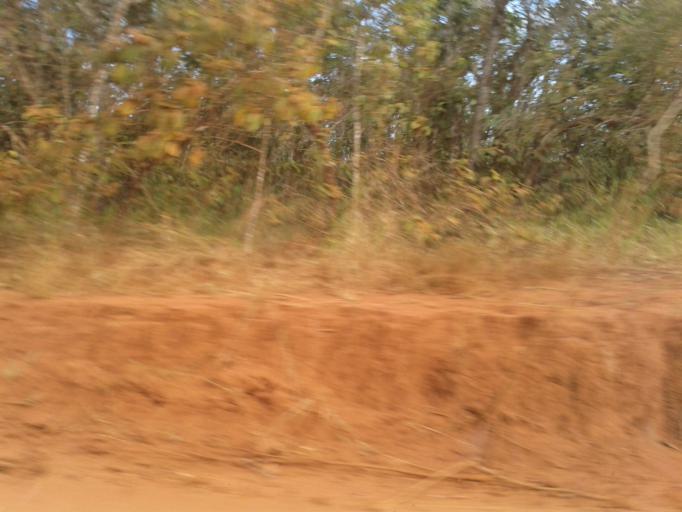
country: BR
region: Minas Gerais
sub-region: Ituiutaba
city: Ituiutaba
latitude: -19.0495
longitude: -49.3645
